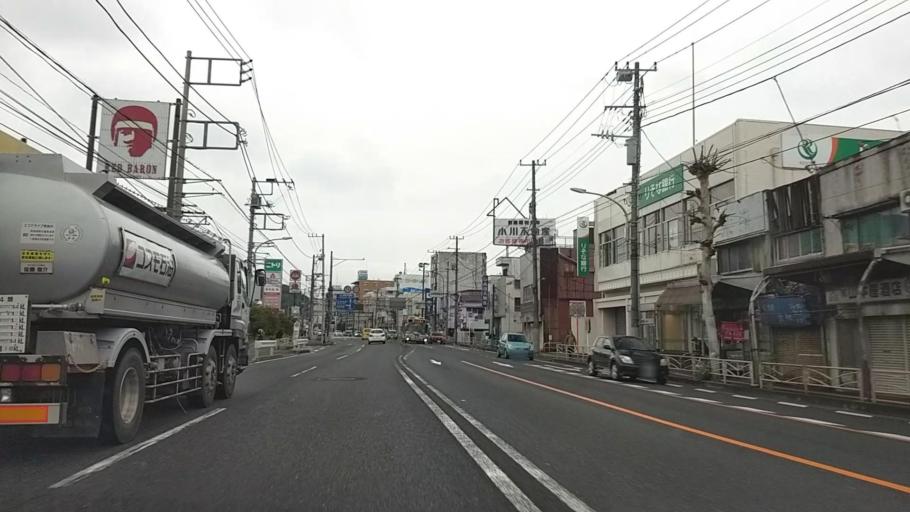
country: JP
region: Kanagawa
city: Yokohama
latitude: 35.4139
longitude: 139.6257
